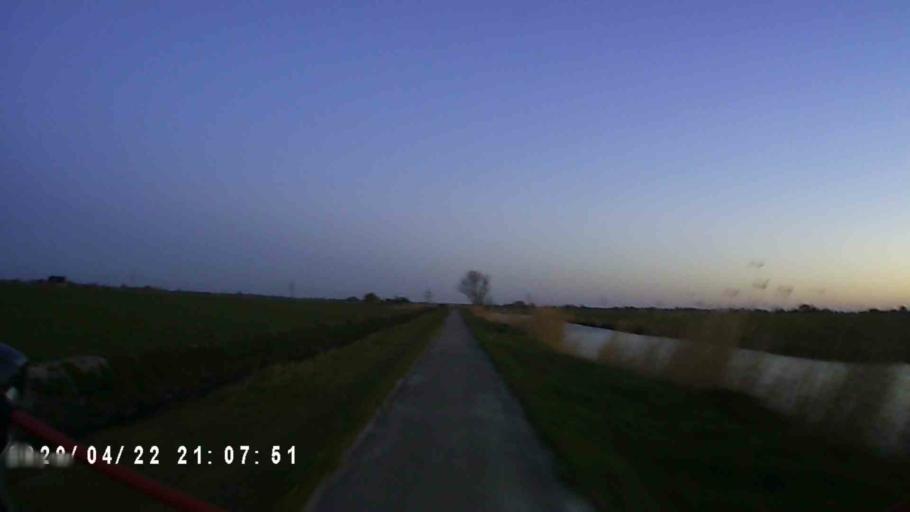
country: NL
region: Groningen
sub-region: Gemeente Winsum
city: Winsum
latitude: 53.3160
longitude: 6.5611
